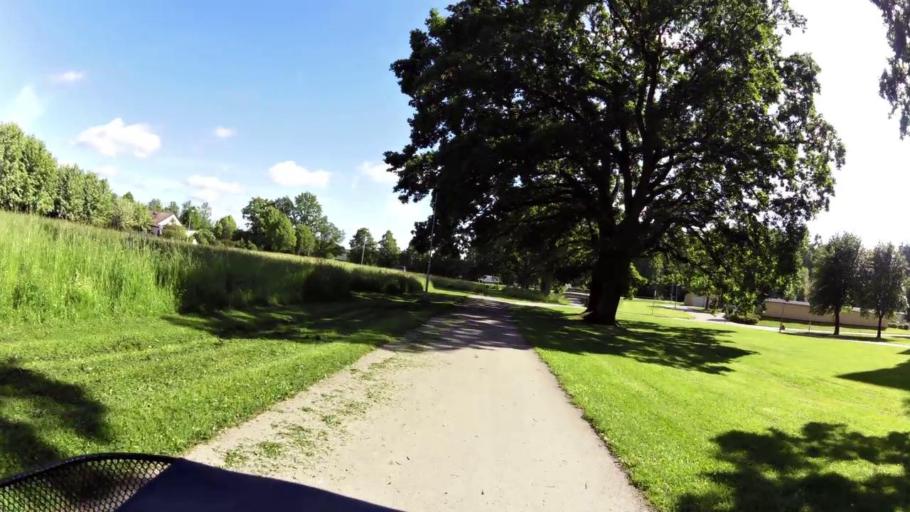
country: SE
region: OEstergoetland
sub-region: Linkopings Kommun
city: Linkoping
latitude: 58.3832
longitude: 15.6404
